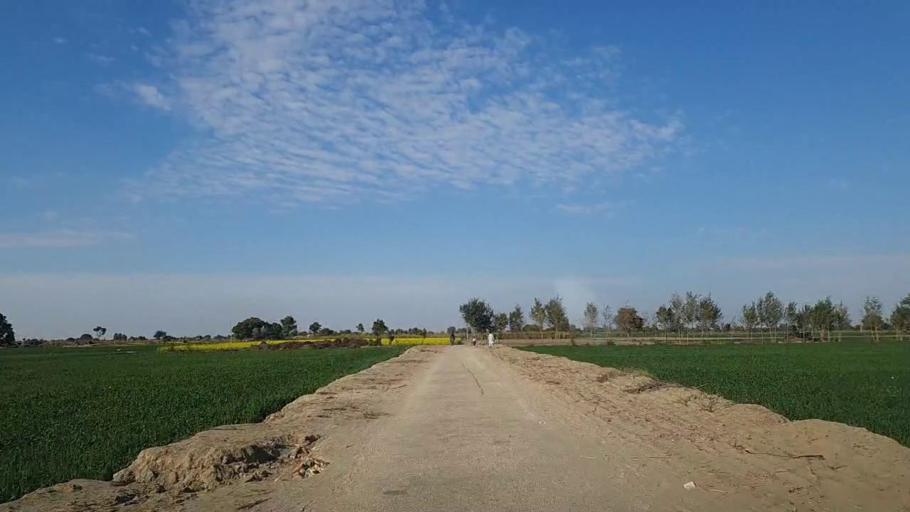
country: PK
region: Sindh
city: Khadro
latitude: 26.3071
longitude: 68.8343
